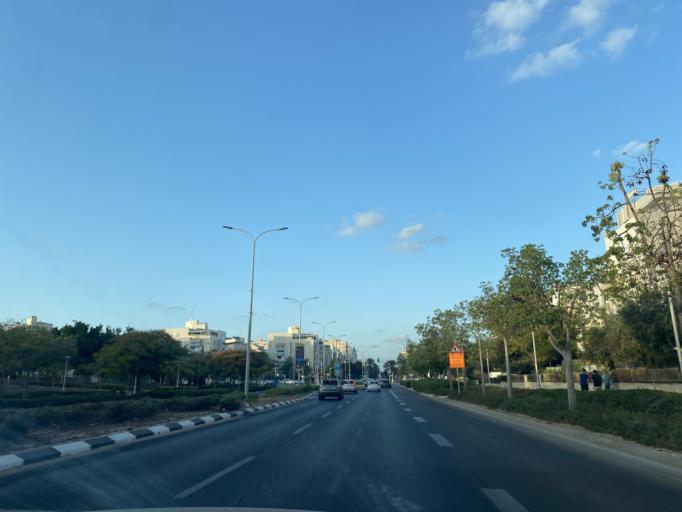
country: IL
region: Southern District
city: Ashdod
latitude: 31.7802
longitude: 34.6423
